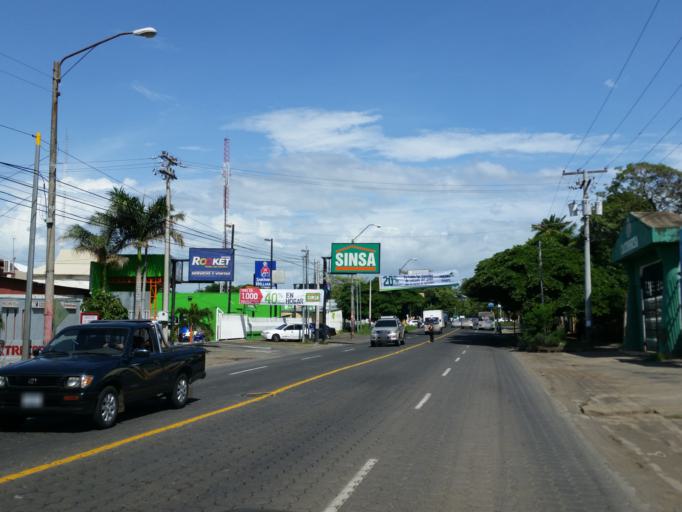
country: NI
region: Managua
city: Managua
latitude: 12.1362
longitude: -86.2863
